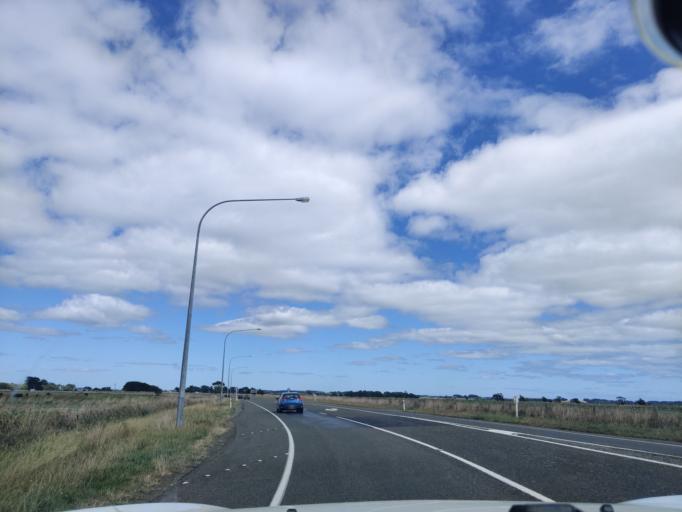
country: NZ
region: Manawatu-Wanganui
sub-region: Palmerston North City
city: Palmerston North
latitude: -40.4126
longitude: 175.4788
